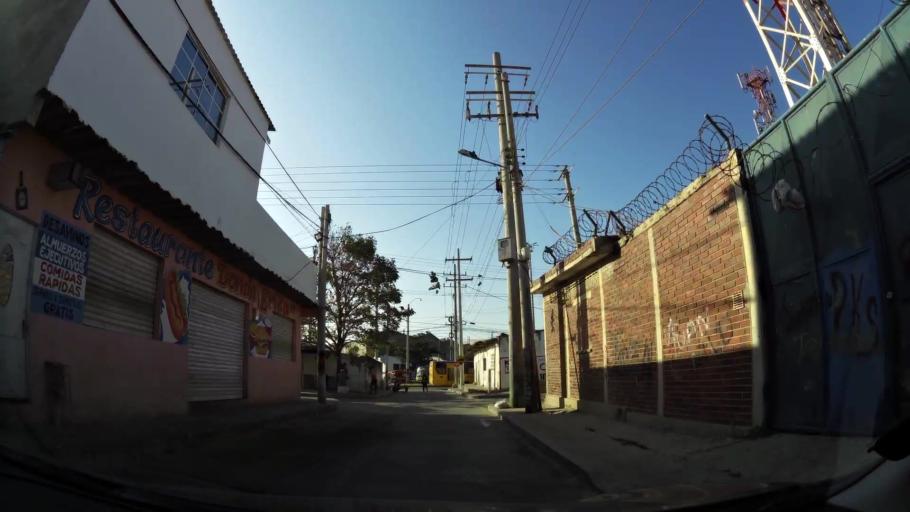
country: CO
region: Atlantico
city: Barranquilla
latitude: 11.0395
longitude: -74.8267
